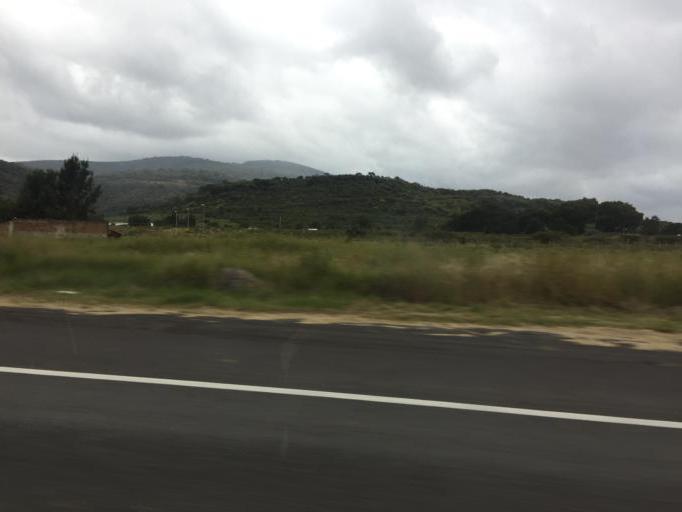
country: MX
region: Jalisco
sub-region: Zapotlanejo
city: La Mezquitera
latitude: 20.5402
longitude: -103.0229
